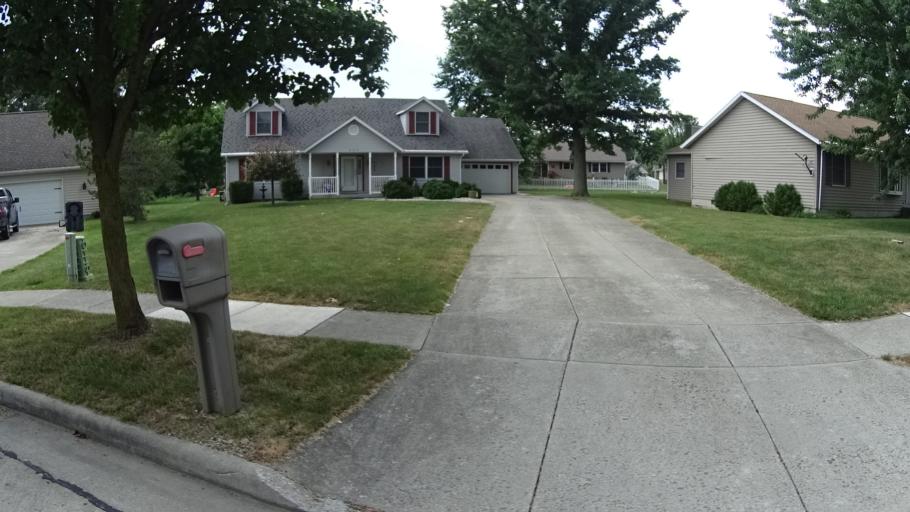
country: US
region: Ohio
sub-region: Erie County
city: Sandusky
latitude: 41.4422
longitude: -82.7656
